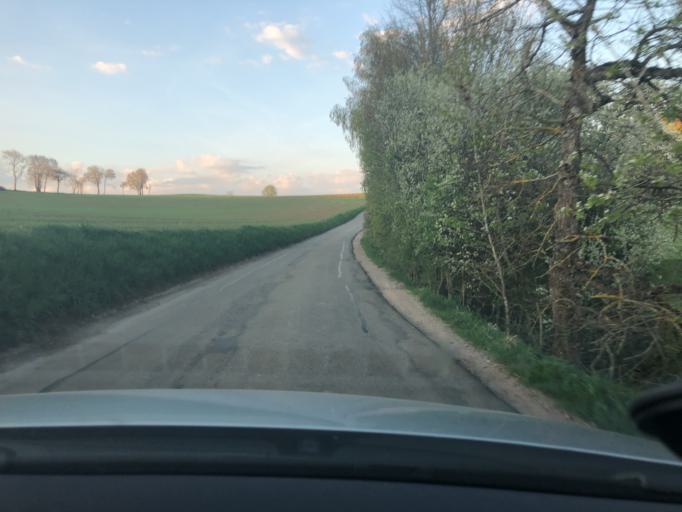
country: DE
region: Baden-Wuerttemberg
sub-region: Freiburg Region
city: Dogern
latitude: 47.6639
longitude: 8.1678
